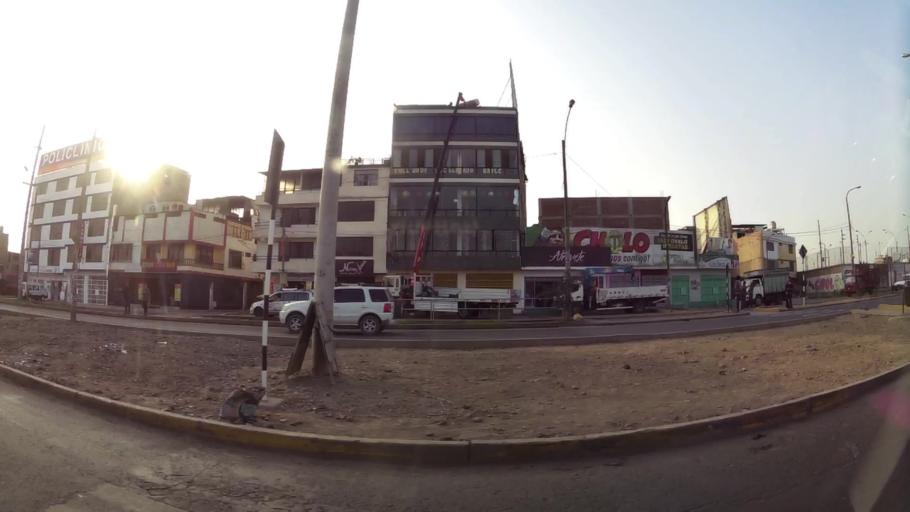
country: PE
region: Lima
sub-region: Lima
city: Independencia
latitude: -11.9461
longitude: -77.0723
